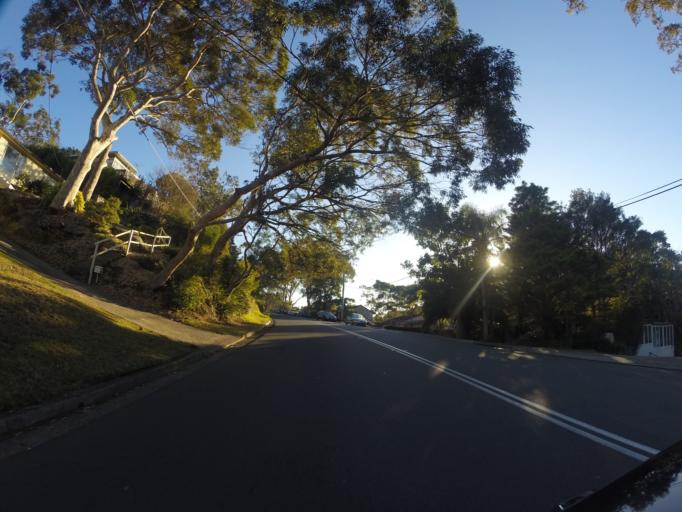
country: AU
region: New South Wales
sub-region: Sutherland Shire
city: Kirrawee
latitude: -34.0473
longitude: 151.0766
